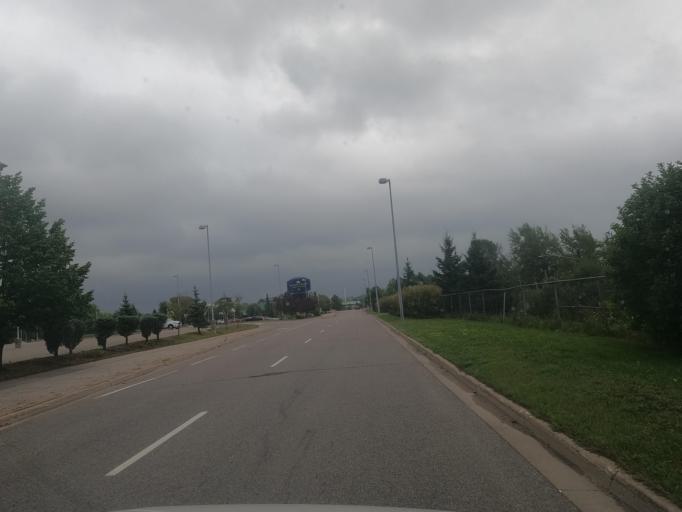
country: CA
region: Ontario
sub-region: Algoma
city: Sault Ste. Marie
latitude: 46.5170
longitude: -84.3473
